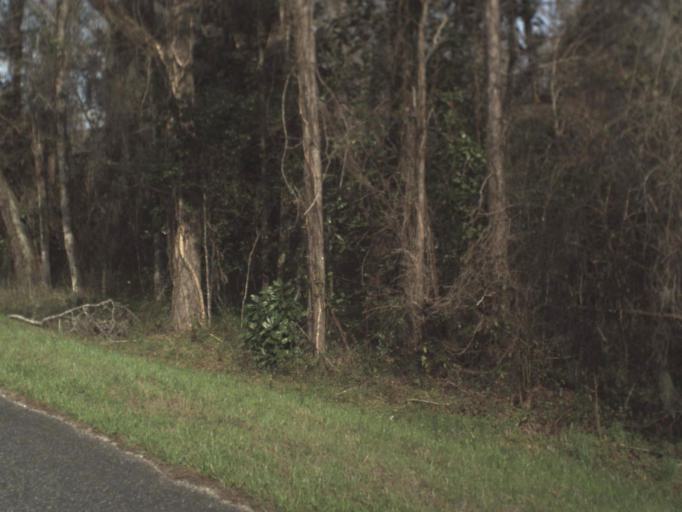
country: US
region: Florida
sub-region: Jefferson County
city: Monticello
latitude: 30.4400
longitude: -83.9042
